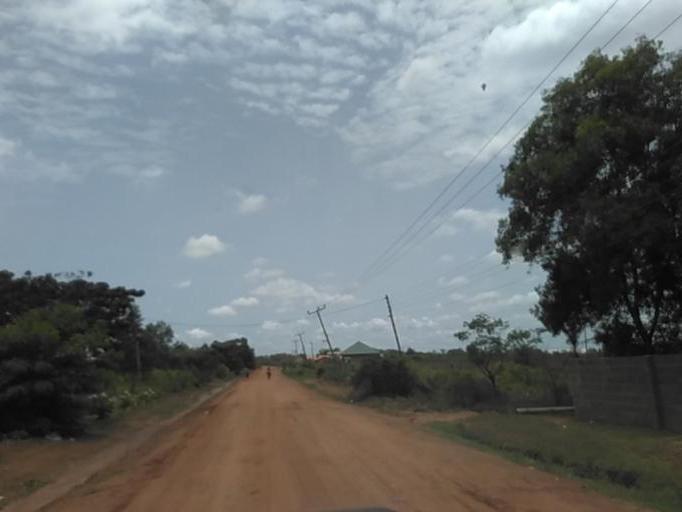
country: GH
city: Akropong
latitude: 6.0328
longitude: 0.3741
